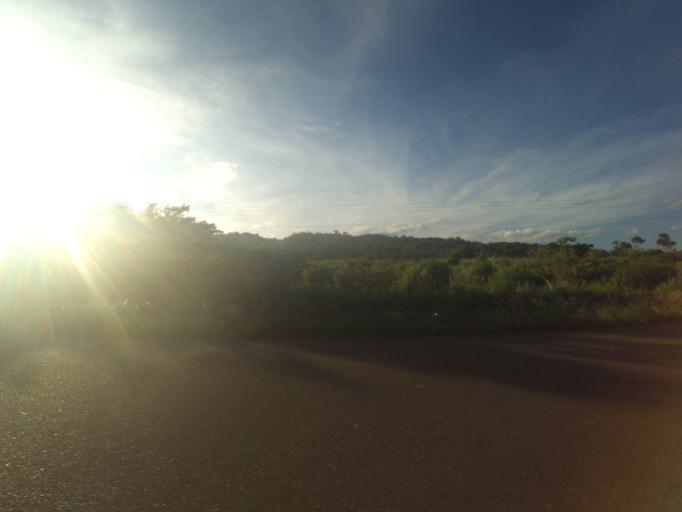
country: BO
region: Santa Cruz
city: Abapo
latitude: -18.8474
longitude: -63.3731
